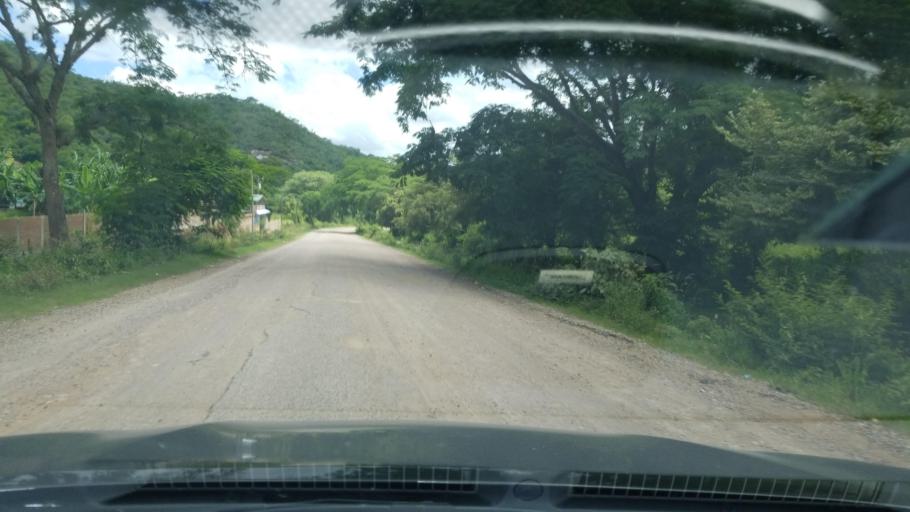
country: HN
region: Francisco Morazan
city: Talanga
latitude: 14.3875
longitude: -87.0734
